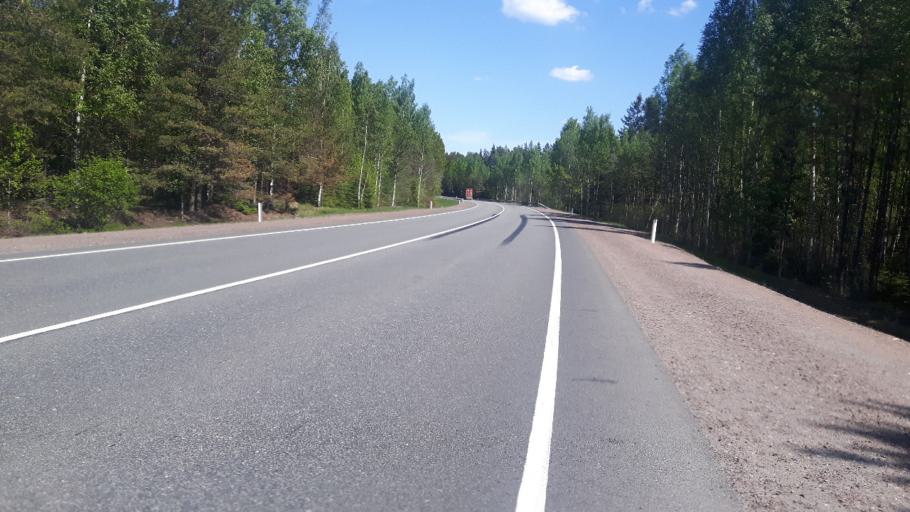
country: FI
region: South Karelia
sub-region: Lappeenranta
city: Ylaemaa
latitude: 60.6265
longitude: 28.2581
